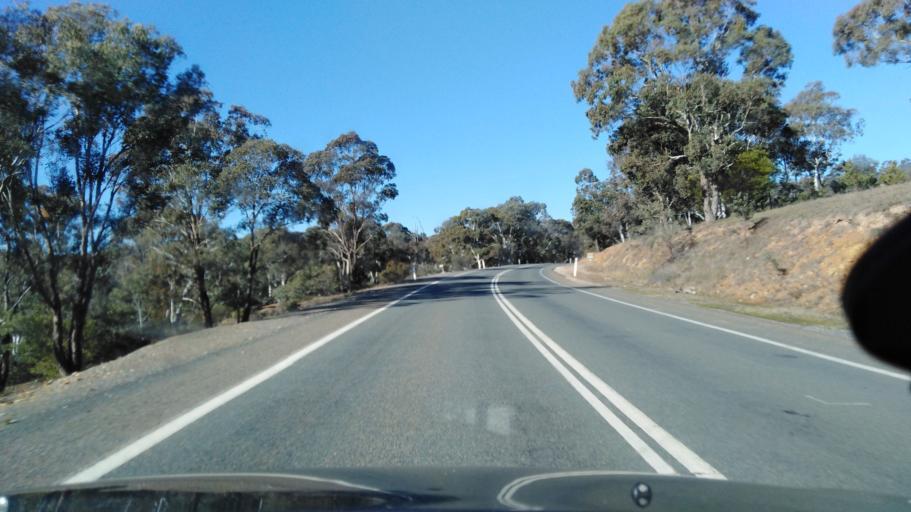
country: AU
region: New South Wales
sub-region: Yass Valley
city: Gundaroo
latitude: -35.1812
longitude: 149.2904
